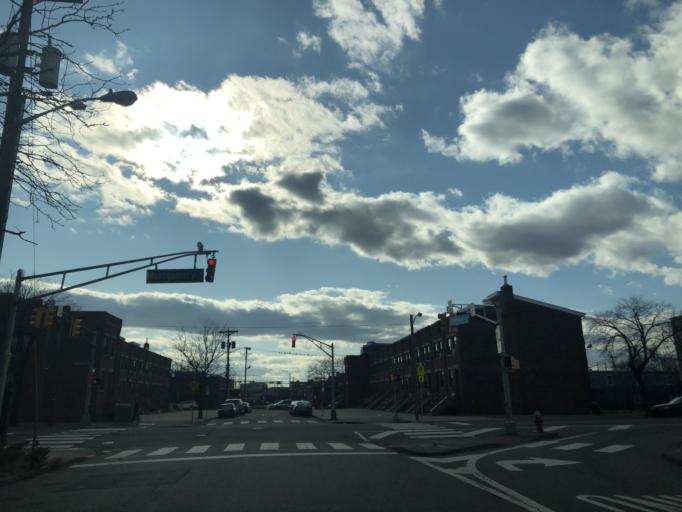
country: US
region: New Jersey
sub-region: Hudson County
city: Jersey City
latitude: 40.7203
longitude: -74.0522
